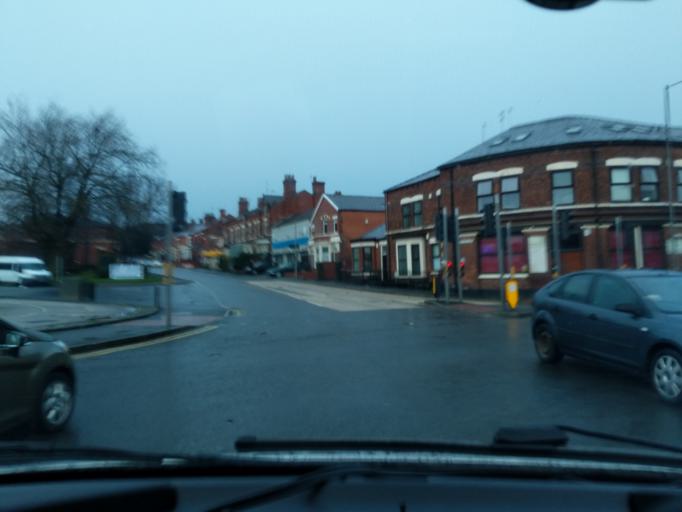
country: GB
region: England
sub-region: St. Helens
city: St Helens
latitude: 53.4571
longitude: -2.7463
